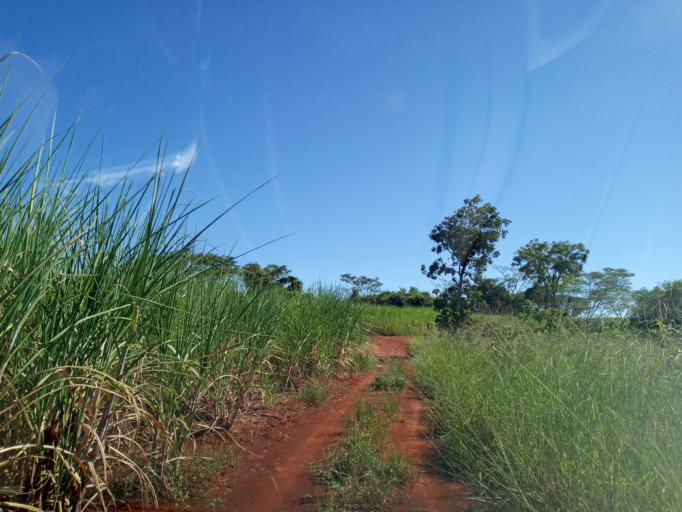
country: BR
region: Goias
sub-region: Itumbiara
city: Itumbiara
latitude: -18.4336
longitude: -49.0905
